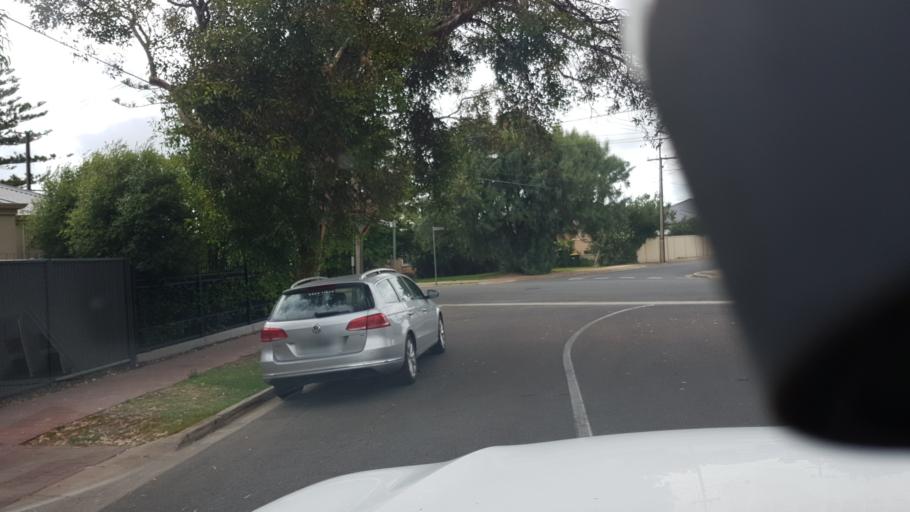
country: AU
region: South Australia
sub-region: Holdfast Bay
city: Glenelg East
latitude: -34.9656
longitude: 138.5207
